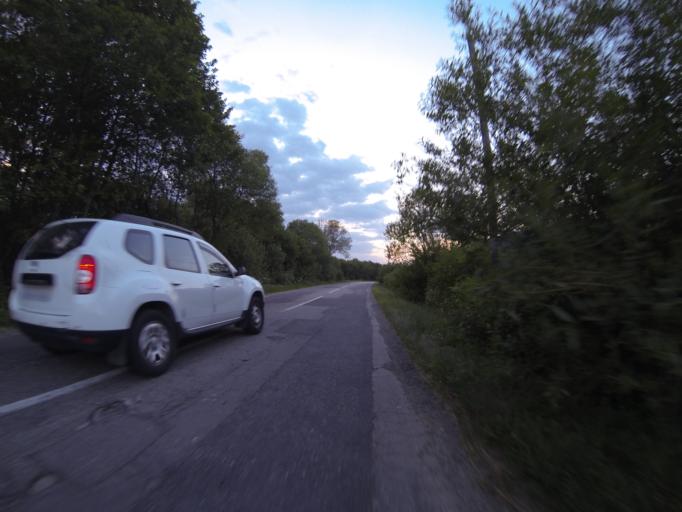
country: RO
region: Brasov
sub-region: Comuna Sinca Noua
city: Sinca Noua
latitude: 45.7336
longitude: 25.2313
